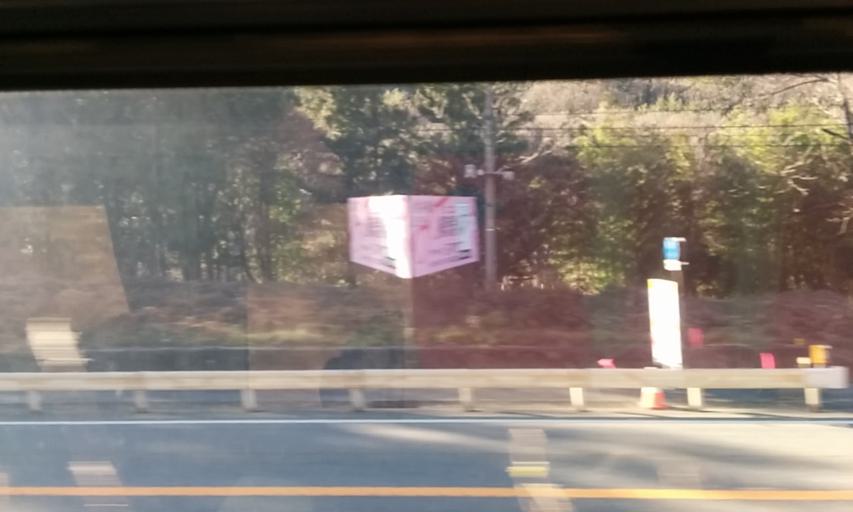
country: JP
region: Nagano
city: Iida
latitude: 35.7165
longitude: 137.7087
